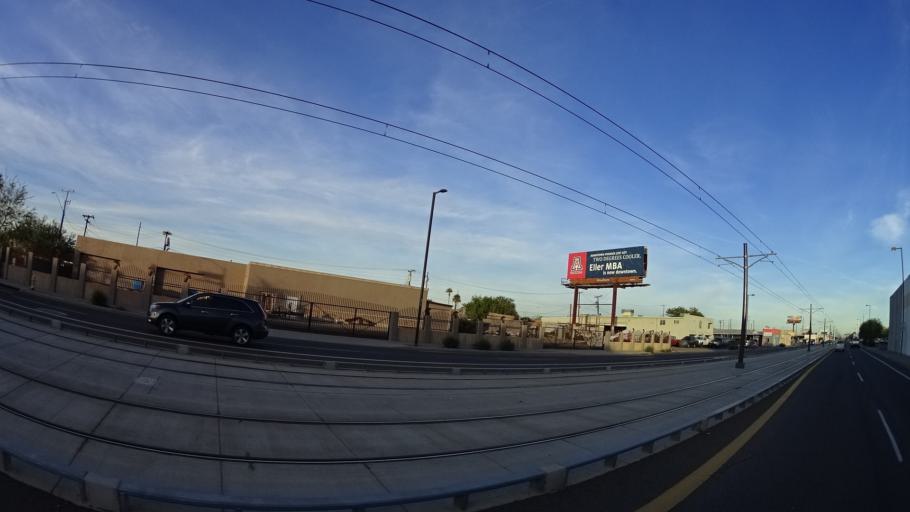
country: US
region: Arizona
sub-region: Maricopa County
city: Phoenix
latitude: 33.4482
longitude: -112.0214
